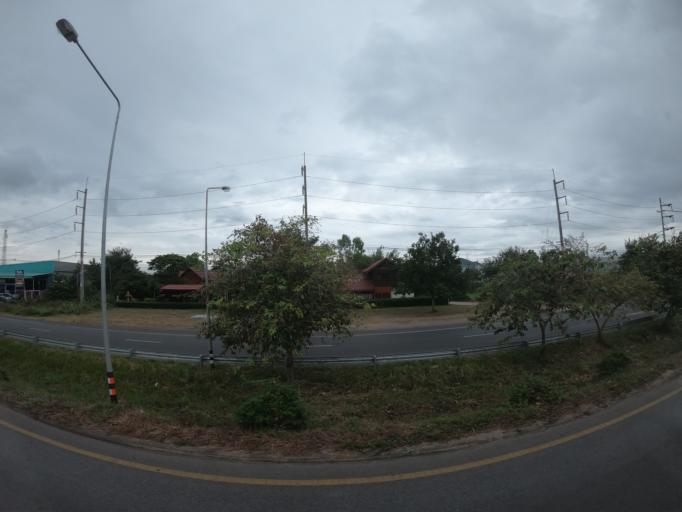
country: TH
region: Roi Et
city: Roi Et
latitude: 16.0456
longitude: 103.6246
